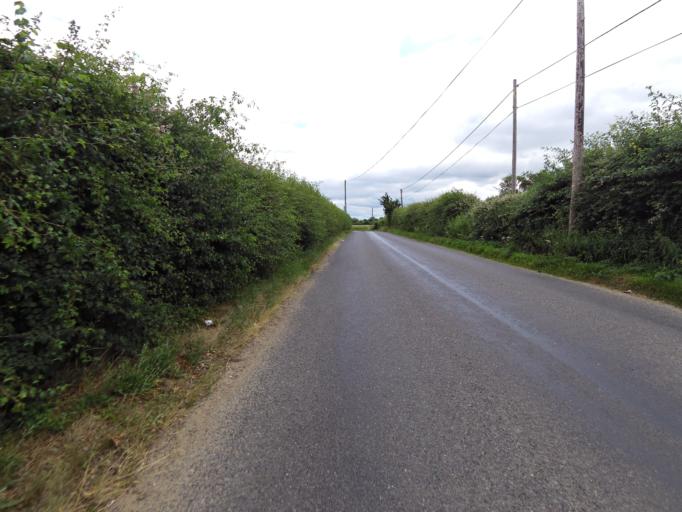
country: GB
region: England
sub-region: Norfolk
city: Harleston
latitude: 52.3983
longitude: 1.2053
